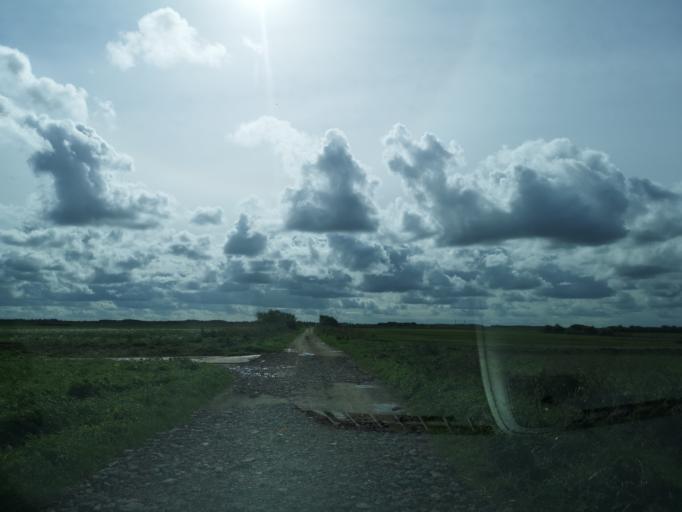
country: DK
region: Central Jutland
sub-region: Ringkobing-Skjern Kommune
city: Tarm
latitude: 55.9341
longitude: 8.5370
